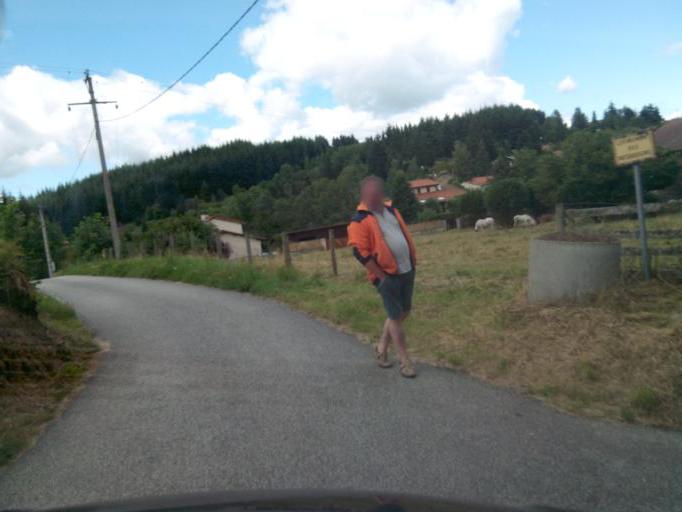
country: FR
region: Rhone-Alpes
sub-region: Departement de la Loire
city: Saint-Bonnet-le-Chateau
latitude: 45.4161
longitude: 4.0040
